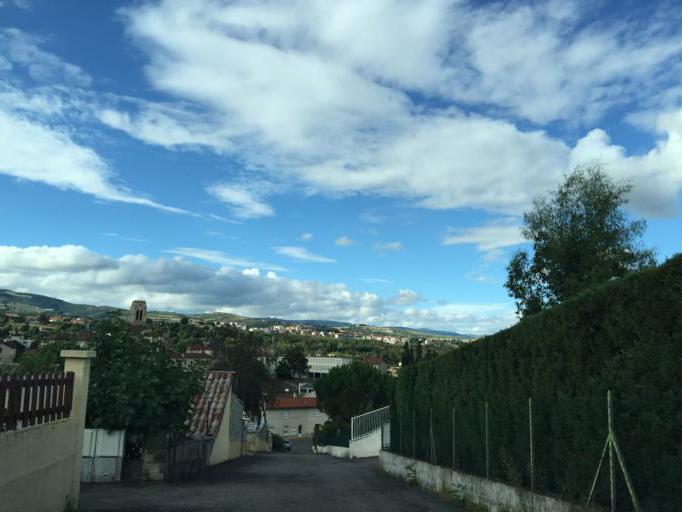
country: FR
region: Rhone-Alpes
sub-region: Departement de la Loire
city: La Grand-Croix
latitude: 45.4829
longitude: 4.5458
